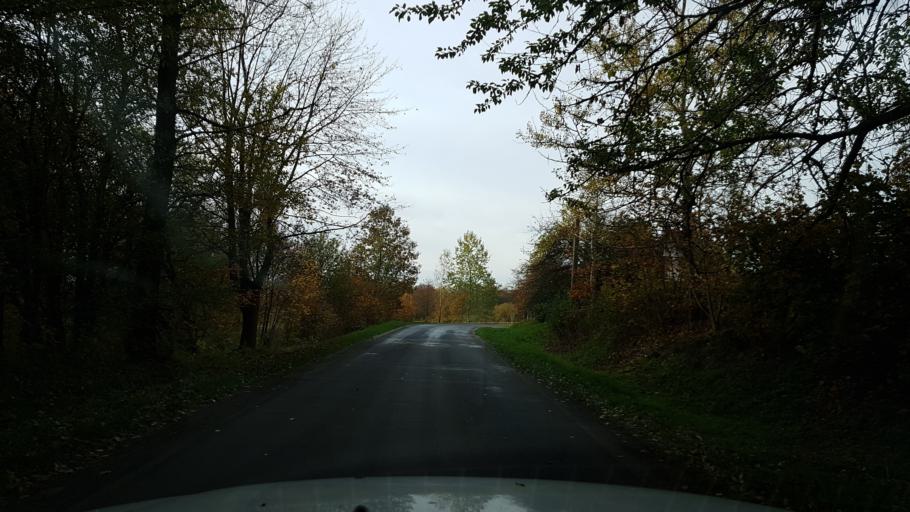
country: PL
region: West Pomeranian Voivodeship
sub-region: Powiat swidwinski
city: Polczyn-Zdroj
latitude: 53.7468
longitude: 16.0464
